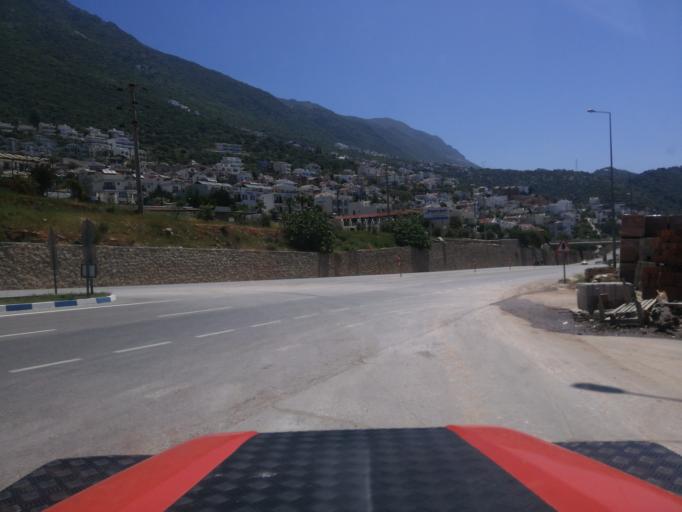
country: TR
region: Antalya
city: Kalkan
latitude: 36.2716
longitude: 29.4135
